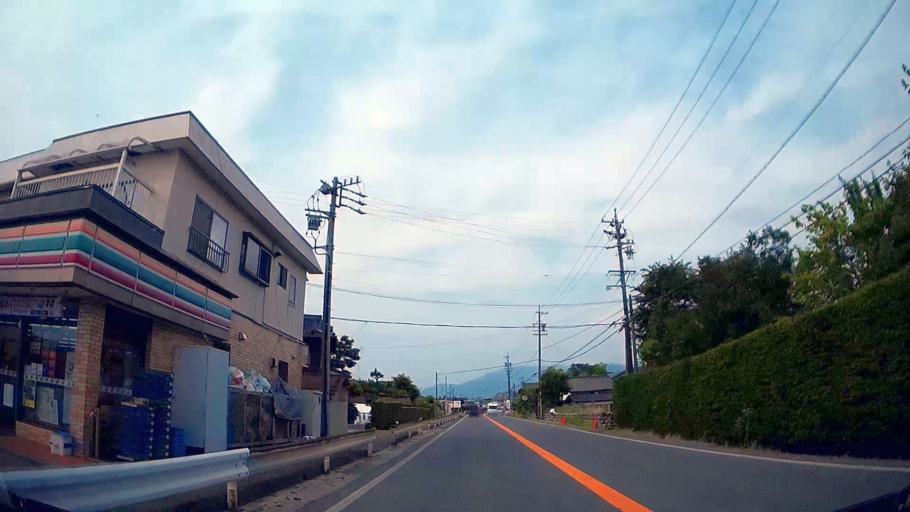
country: JP
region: Nagano
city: Iida
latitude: 35.5909
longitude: 137.9142
